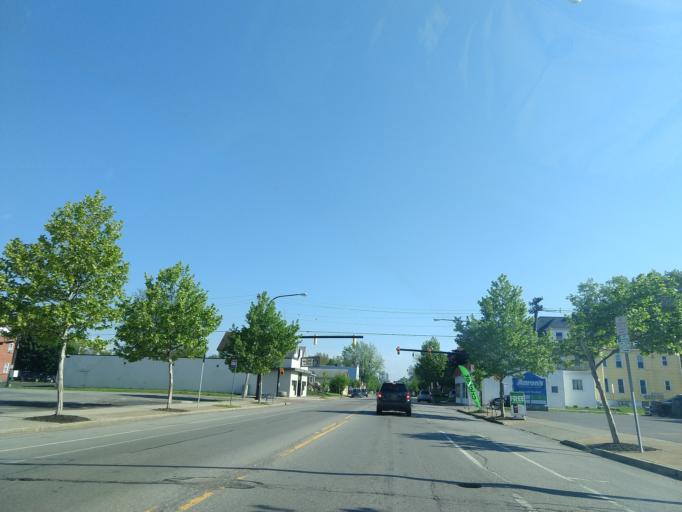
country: US
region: New York
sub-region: Erie County
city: Lackawanna
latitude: 42.8377
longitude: -78.8239
